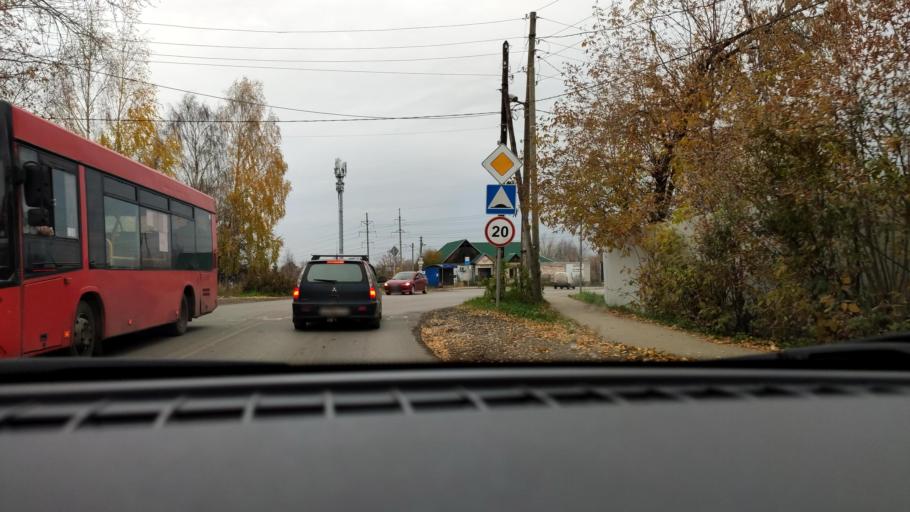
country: RU
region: Perm
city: Perm
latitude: 58.0113
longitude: 56.3201
